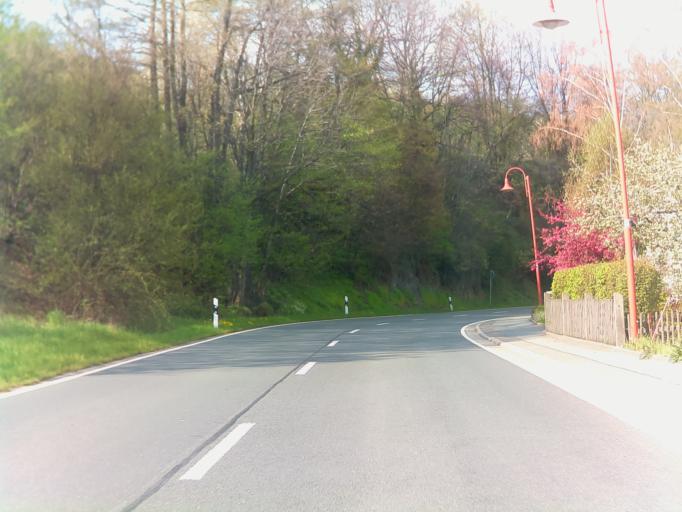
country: DE
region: Thuringia
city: Probstzella
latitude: 50.5822
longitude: 11.3959
